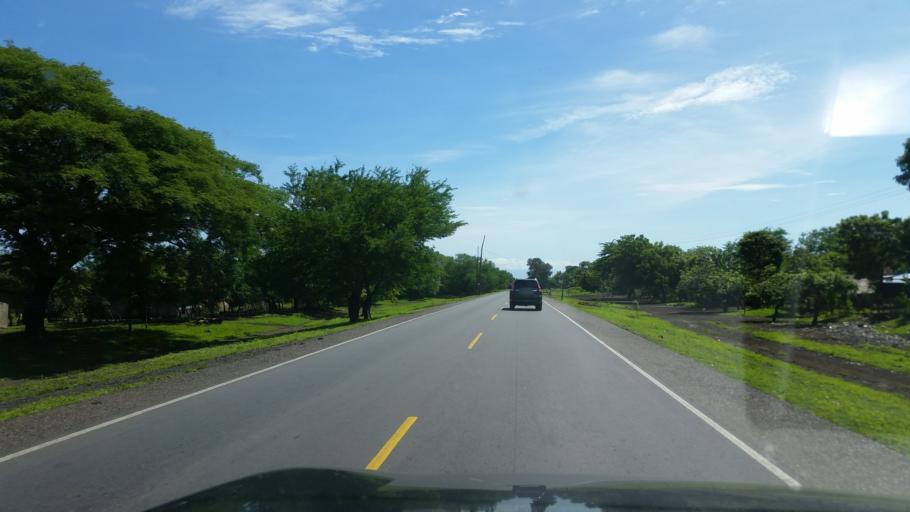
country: NI
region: Chinandega
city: El Viejo
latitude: 12.7515
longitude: -87.0674
